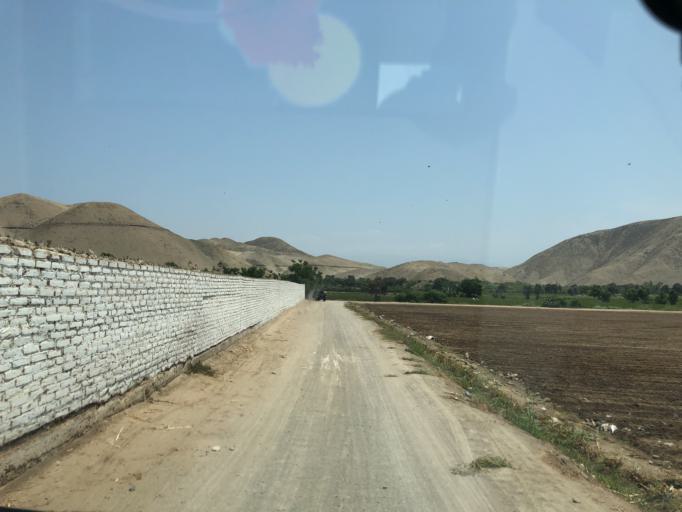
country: PE
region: Lima
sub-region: Provincia de Canete
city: Quilmana
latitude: -12.9997
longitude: -76.4469
